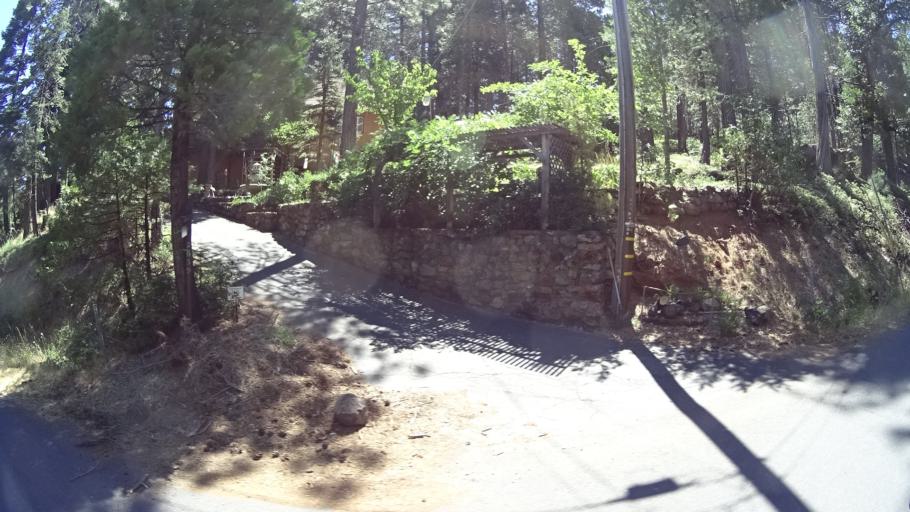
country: US
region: California
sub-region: Calaveras County
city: Arnold
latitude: 38.2317
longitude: -120.3430
